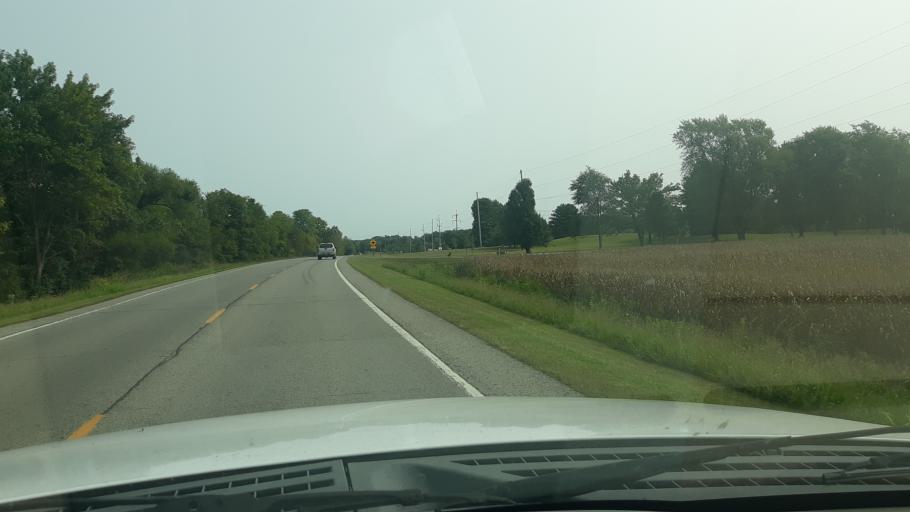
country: US
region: Illinois
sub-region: White County
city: Norris City
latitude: 37.9782
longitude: -88.3172
